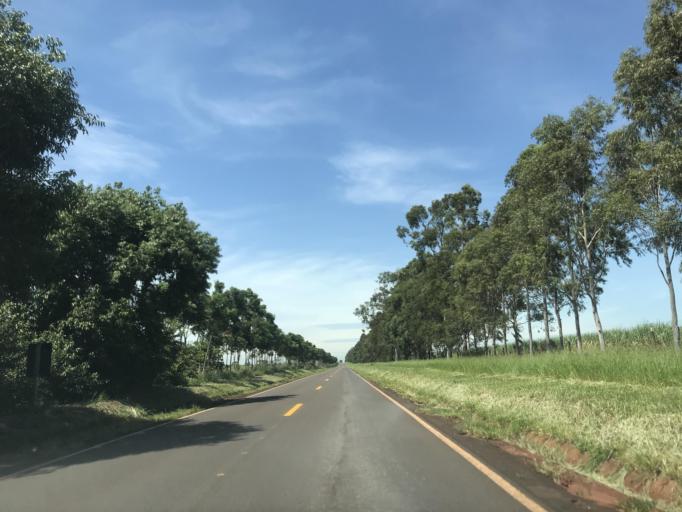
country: BR
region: Parana
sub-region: Paranavai
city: Nova Aurora
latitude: -22.8498
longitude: -52.6577
